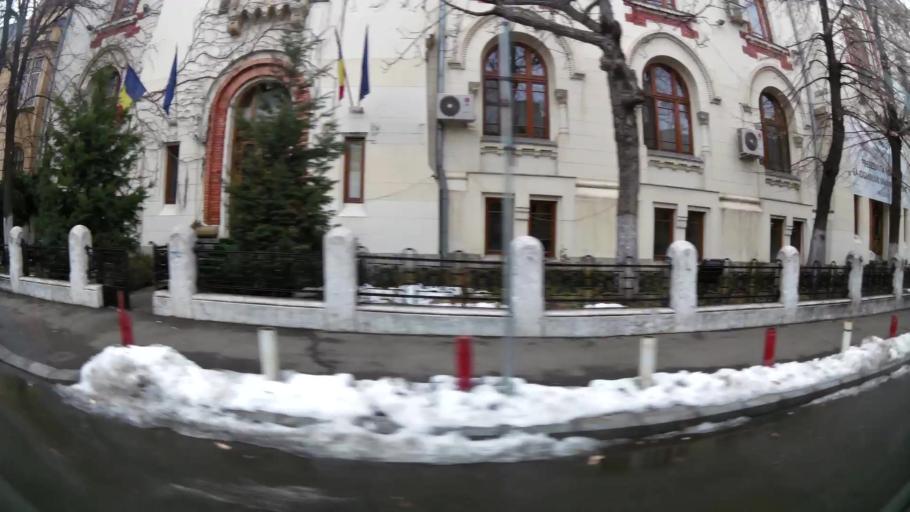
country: RO
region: Bucuresti
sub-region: Municipiul Bucuresti
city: Bucuresti
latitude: 44.4416
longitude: 26.0889
